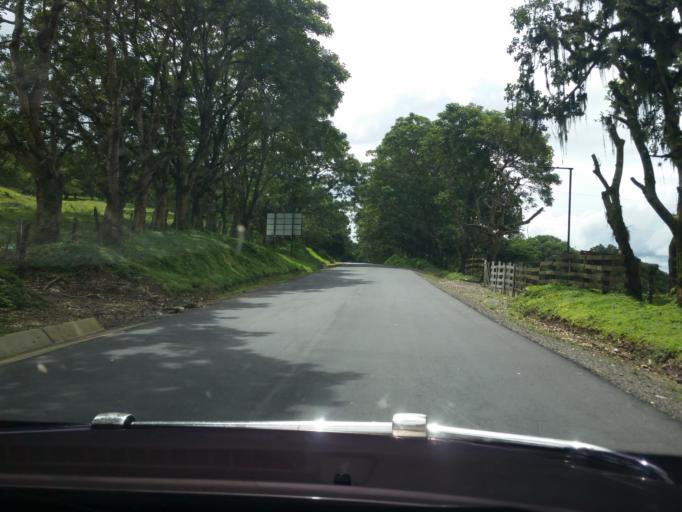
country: NI
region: Jinotega
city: Jinotega
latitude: 13.1536
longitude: -85.9537
